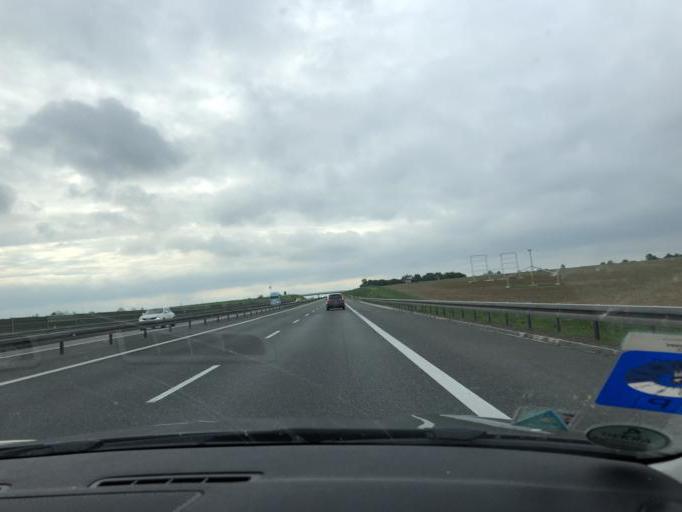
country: PL
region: Opole Voivodeship
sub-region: Powiat krapkowicki
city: Gogolin
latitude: 50.4801
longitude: 18.0613
